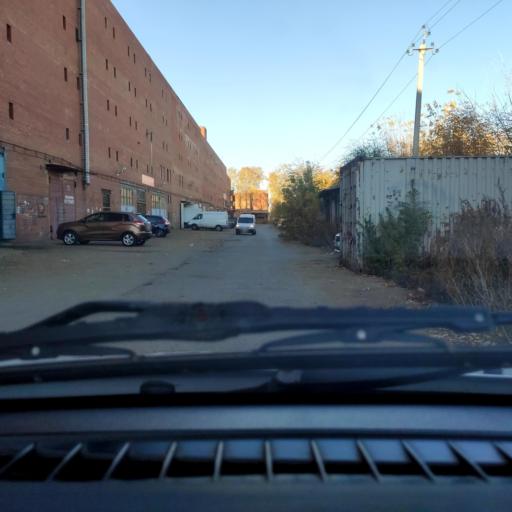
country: RU
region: Samara
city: Tol'yatti
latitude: 53.5398
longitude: 49.3039
